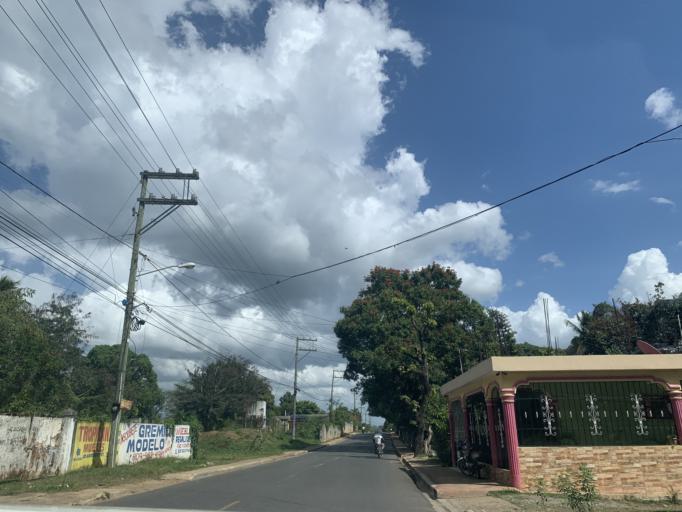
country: DO
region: Monte Plata
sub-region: Yamasa
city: Yamasa
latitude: 18.7721
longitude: -70.0141
